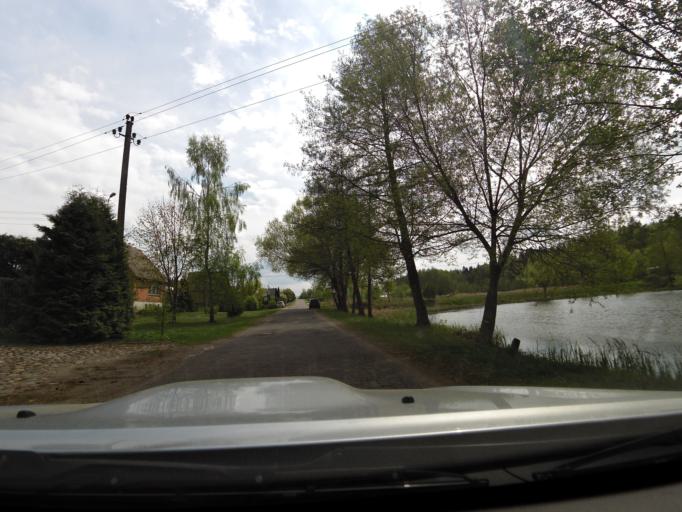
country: LT
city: Salcininkai
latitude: 54.4309
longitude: 25.3099
